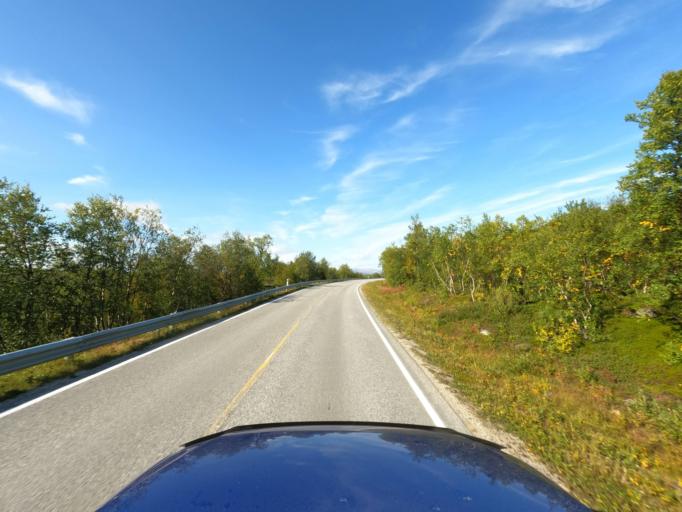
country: NO
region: Finnmark Fylke
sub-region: Porsanger
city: Lakselv
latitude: 69.7677
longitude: 25.1713
